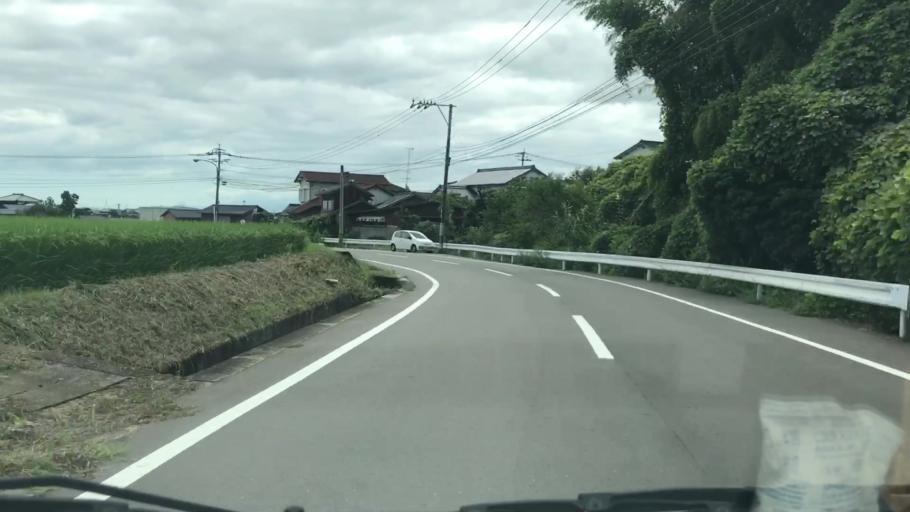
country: JP
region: Saga Prefecture
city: Takeocho-takeo
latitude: 33.2300
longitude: 130.1449
